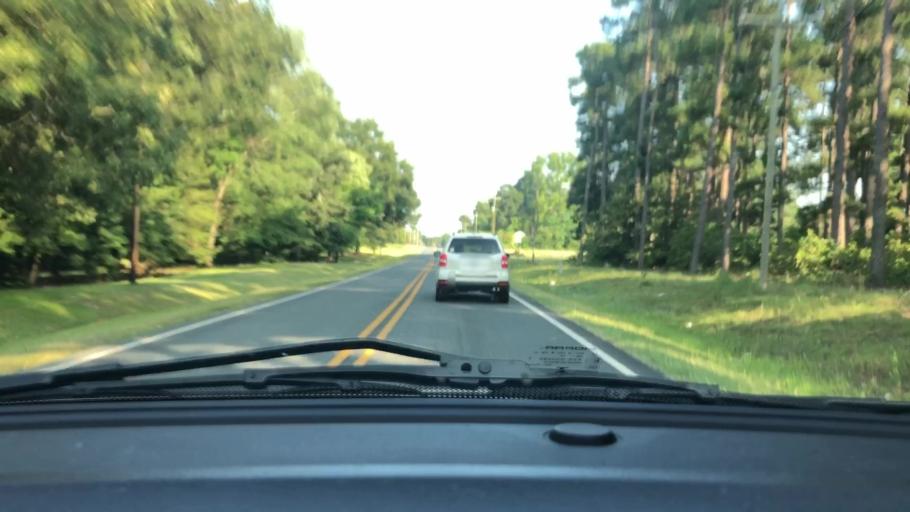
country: US
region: North Carolina
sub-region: Lee County
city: Broadway
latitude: 35.3535
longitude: -79.0760
